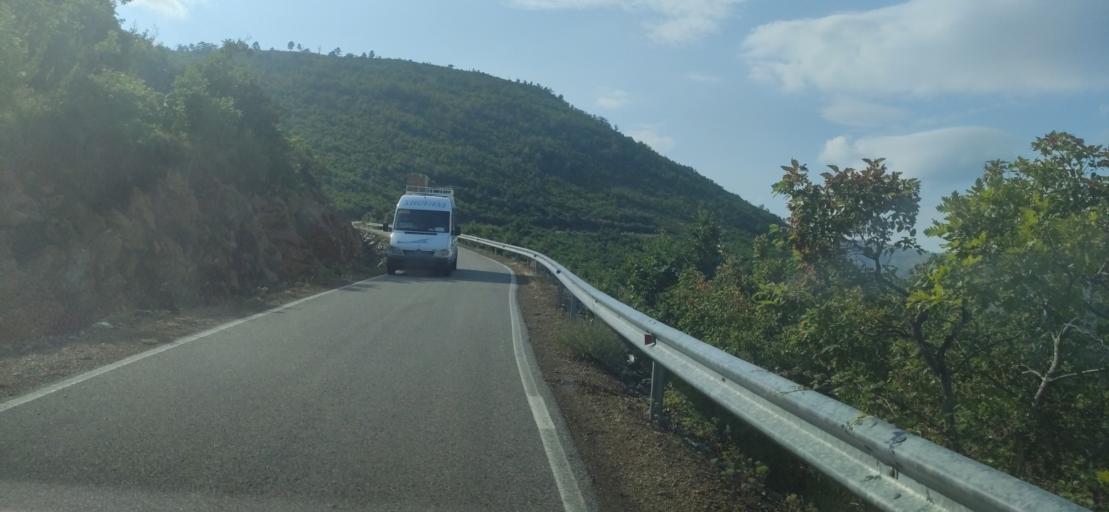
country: AL
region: Shkoder
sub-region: Rrethi i Pukes
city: Iballe
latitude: 42.1718
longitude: 20.0009
